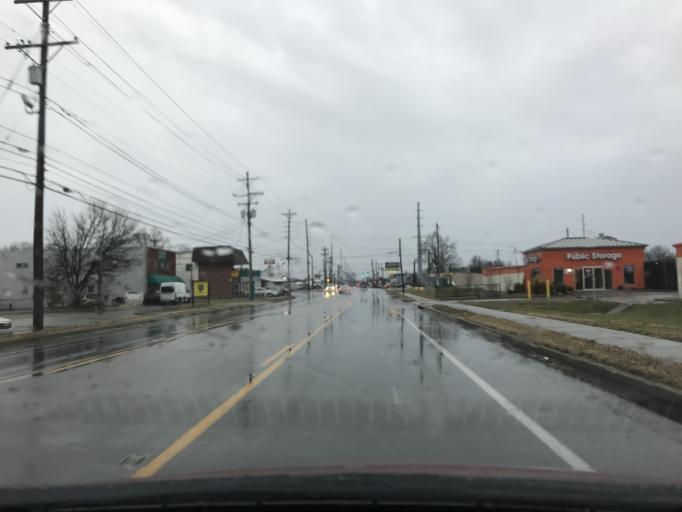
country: US
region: Kentucky
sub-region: Jefferson County
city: Buechel
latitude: 38.1962
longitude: -85.6550
